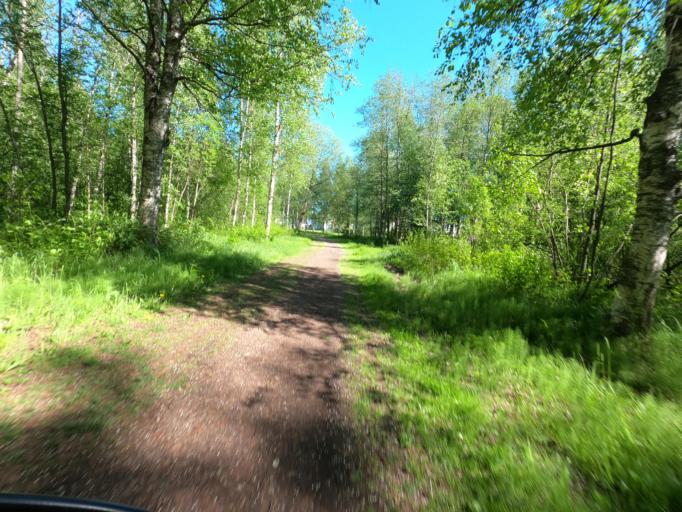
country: FI
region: North Karelia
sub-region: Joensuu
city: Joensuu
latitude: 62.6049
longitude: 29.8155
